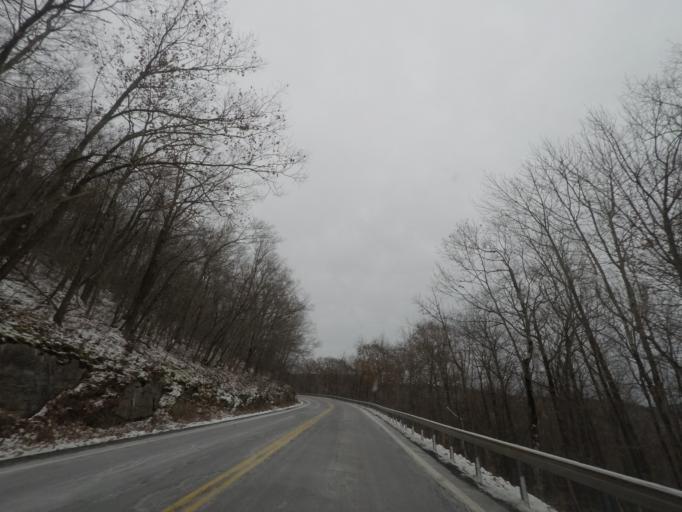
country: US
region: Massachusetts
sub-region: Berkshire County
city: Williamstown
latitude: 42.7310
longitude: -73.2748
